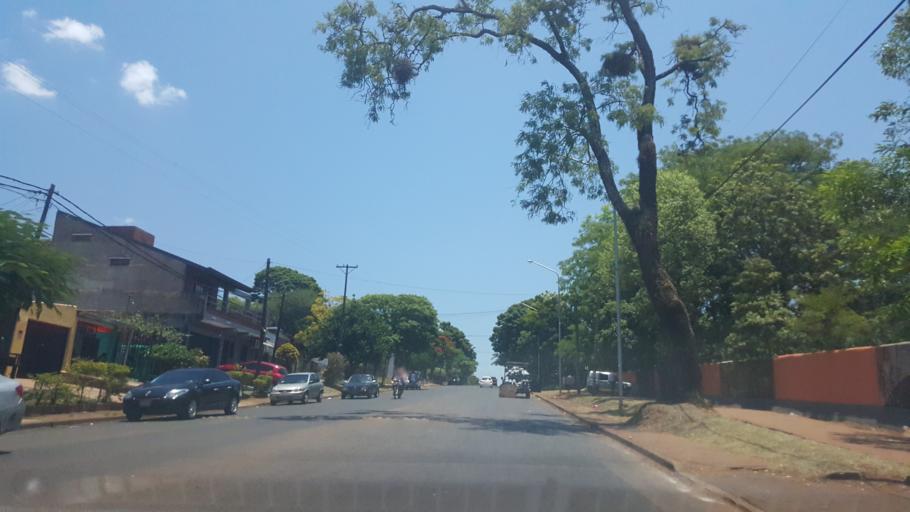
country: AR
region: Misiones
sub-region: Departamento de Capital
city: Posadas
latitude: -27.4052
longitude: -55.8955
